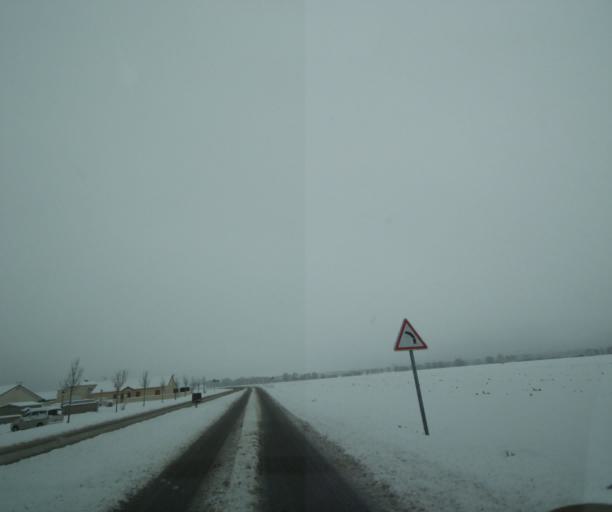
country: FR
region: Champagne-Ardenne
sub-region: Departement de la Haute-Marne
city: Saint-Dizier
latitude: 48.5795
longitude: 4.9057
